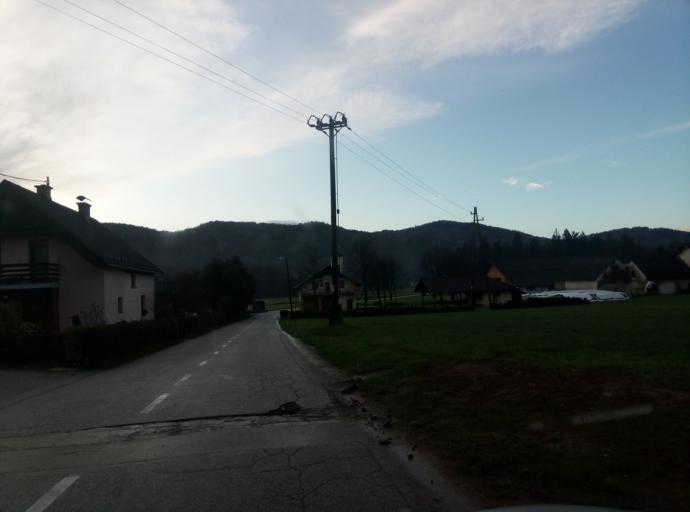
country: SI
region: Vodice
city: Vodice
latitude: 46.1690
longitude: 14.5189
